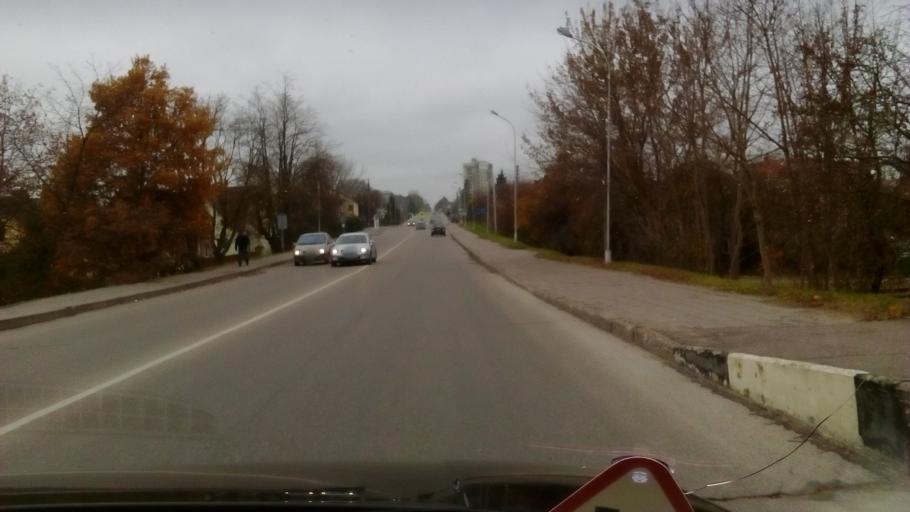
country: LT
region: Marijampoles apskritis
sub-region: Marijampole Municipality
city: Marijampole
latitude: 54.5594
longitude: 23.3450
